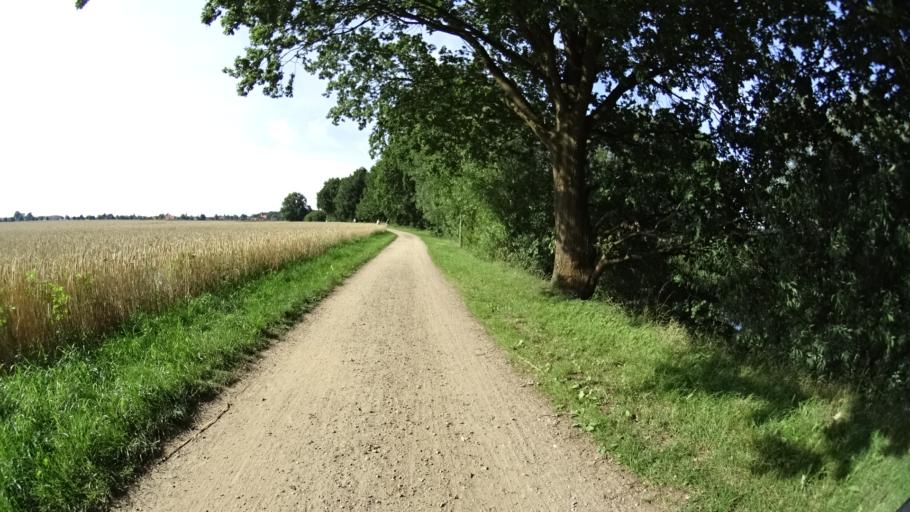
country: DE
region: Lower Saxony
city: Bardowick
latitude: 53.2836
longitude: 10.4052
